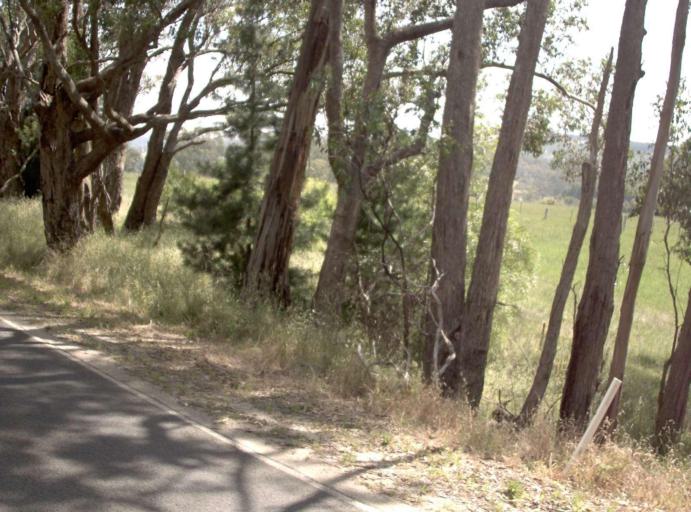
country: AU
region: Victoria
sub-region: Latrobe
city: Traralgon
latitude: -38.2931
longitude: 146.5389
